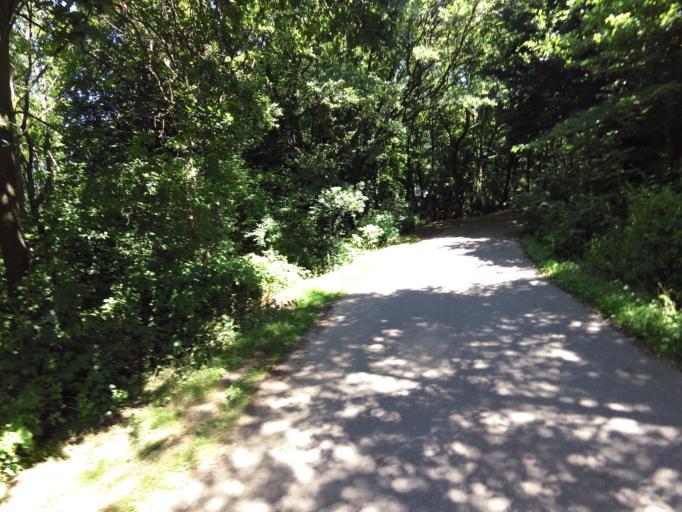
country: NL
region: Limburg
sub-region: Gemeente Kerkrade
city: Kerkrade
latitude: 50.8700
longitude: 6.0448
